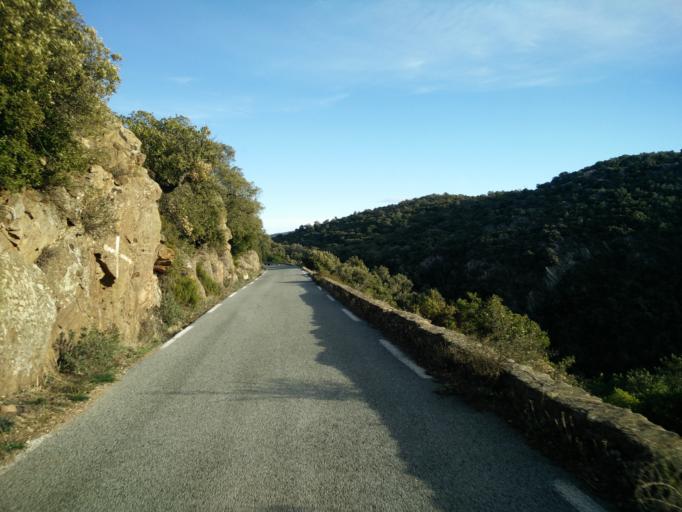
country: FR
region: Provence-Alpes-Cote d'Azur
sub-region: Departement du Var
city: Collobrieres
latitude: 43.1888
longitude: 6.3205
